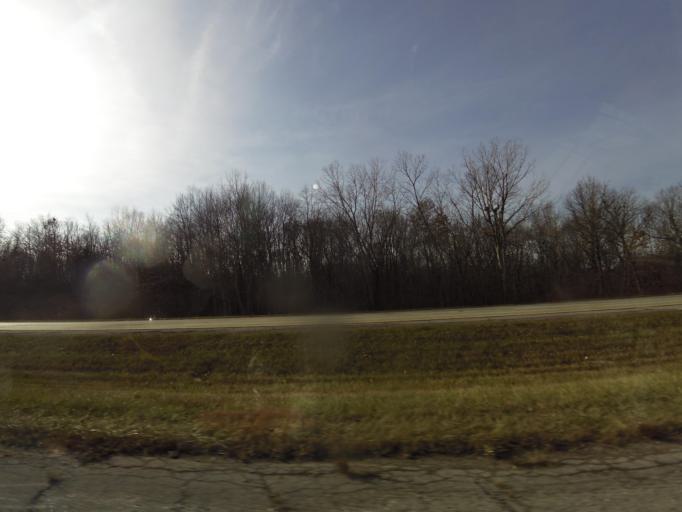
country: US
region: Illinois
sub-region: De Witt County
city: Clinton
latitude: 40.1317
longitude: -88.9694
